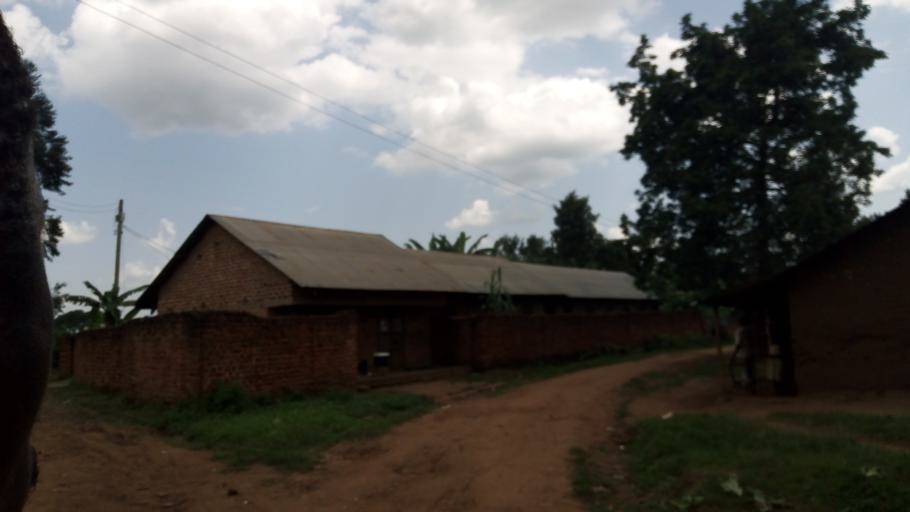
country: UG
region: Eastern Region
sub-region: Mbale District
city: Mbale
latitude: 1.0248
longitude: 34.1752
